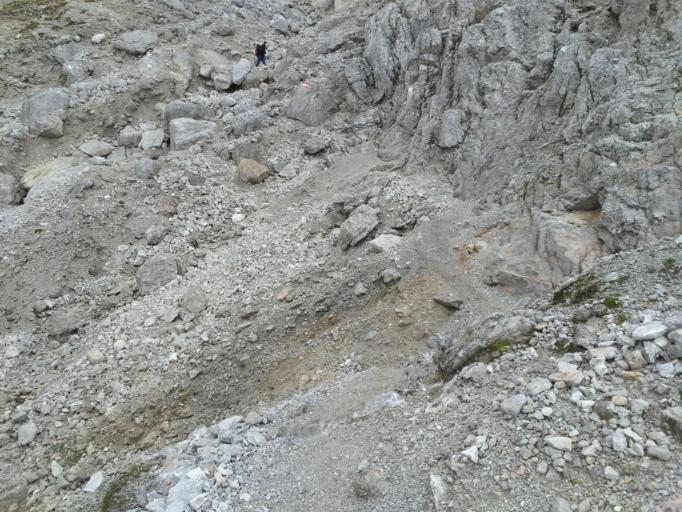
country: AT
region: Styria
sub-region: Politischer Bezirk Liezen
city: Schladming
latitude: 47.4623
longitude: 13.6259
